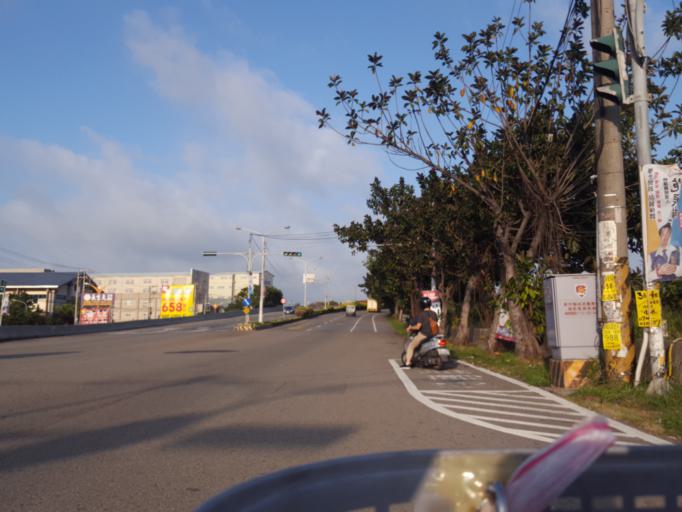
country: TW
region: Taiwan
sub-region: Hsinchu
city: Zhubei
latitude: 24.8853
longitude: 121.0145
